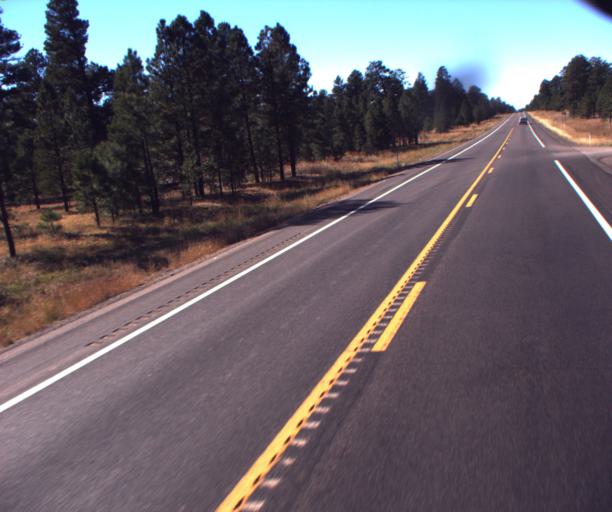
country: US
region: Arizona
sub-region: Apache County
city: Saint Michaels
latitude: 35.6868
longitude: -109.2431
